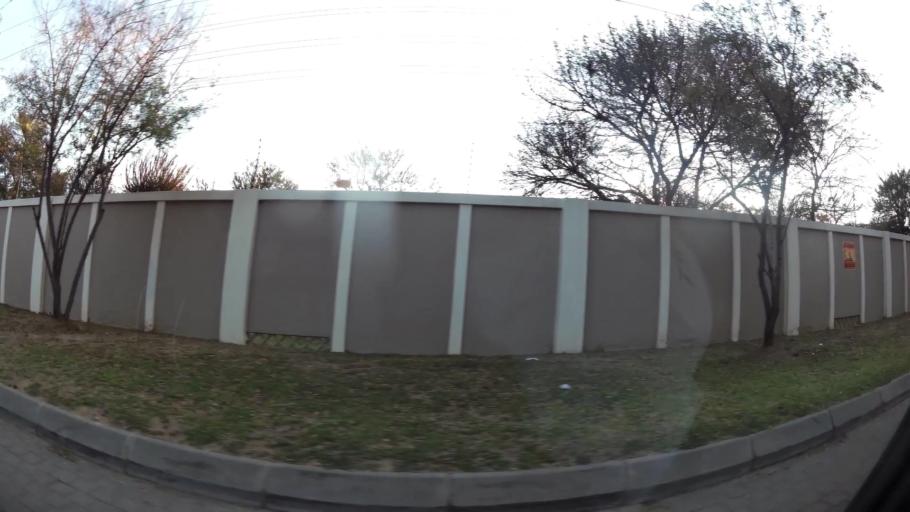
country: ZA
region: Gauteng
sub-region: City of Johannesburg Metropolitan Municipality
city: Diepsloot
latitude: -26.0480
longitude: 27.9741
